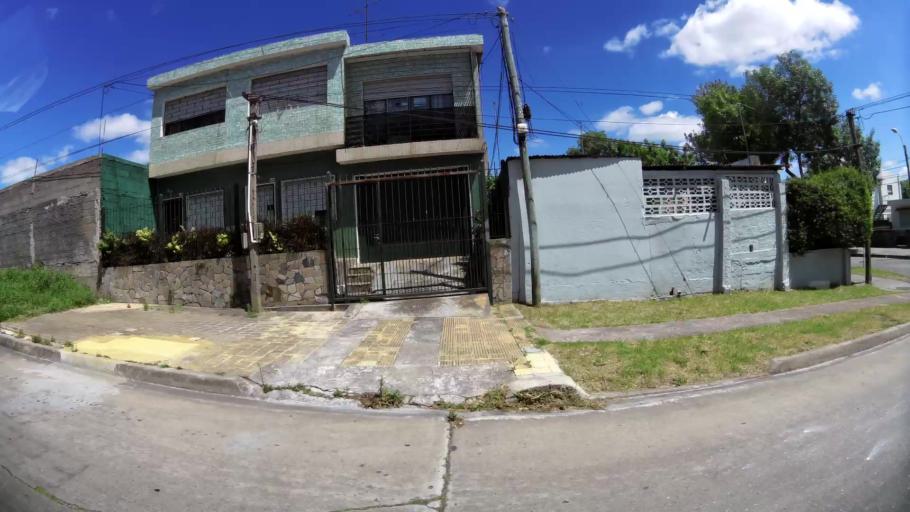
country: UY
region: Montevideo
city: Montevideo
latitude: -34.8597
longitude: -56.1309
